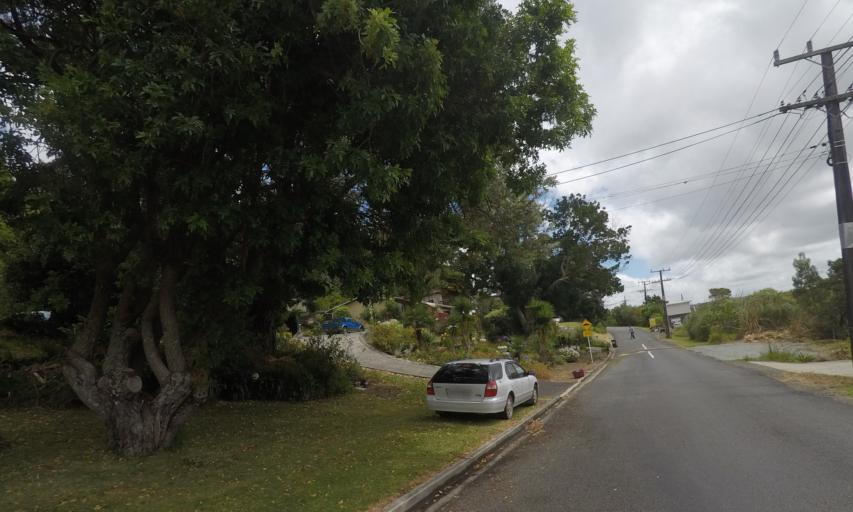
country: NZ
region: Northland
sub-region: Whangarei
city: Whangarei
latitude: -35.7421
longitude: 174.3623
